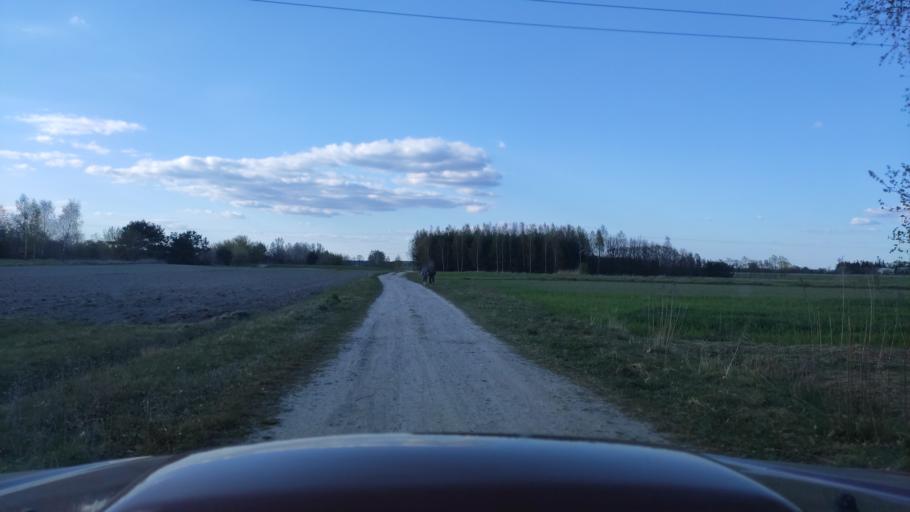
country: PL
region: Masovian Voivodeship
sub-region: Powiat zwolenski
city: Zwolen
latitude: 51.3665
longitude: 21.5754
